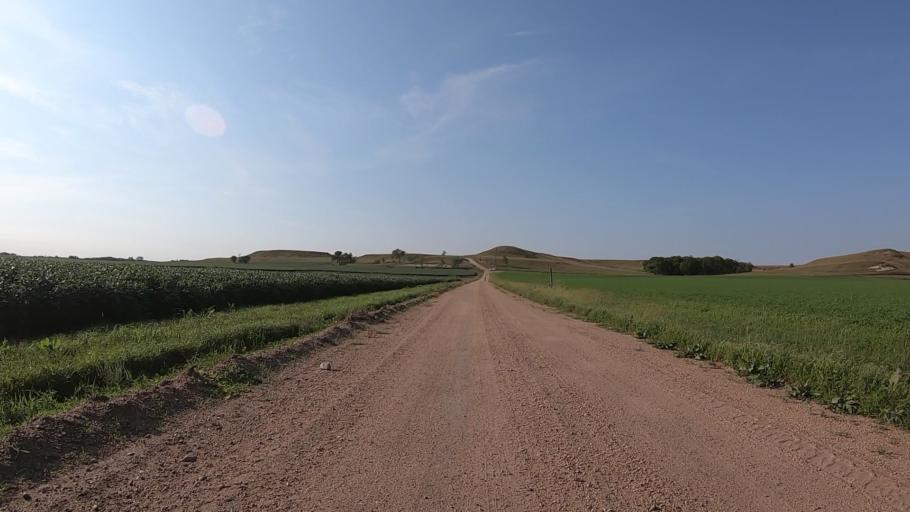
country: US
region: Kansas
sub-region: Marshall County
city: Blue Rapids
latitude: 39.6540
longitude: -96.8815
